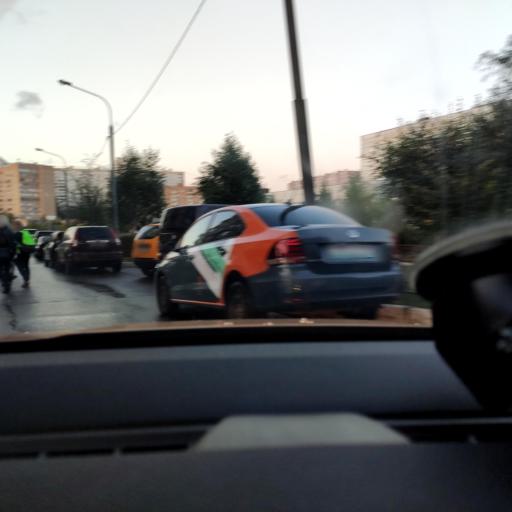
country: RU
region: Moscow
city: Yaroslavskiy
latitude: 55.8964
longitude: 37.7139
